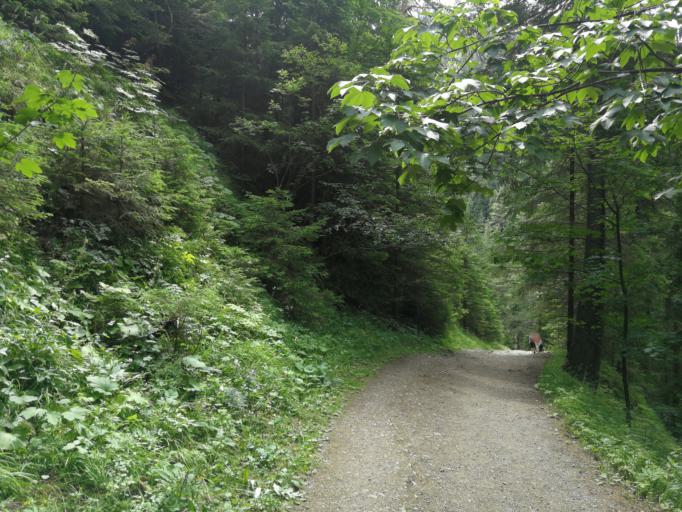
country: SK
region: Zilinsky
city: Tvrdosin
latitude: 49.1973
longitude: 19.5419
